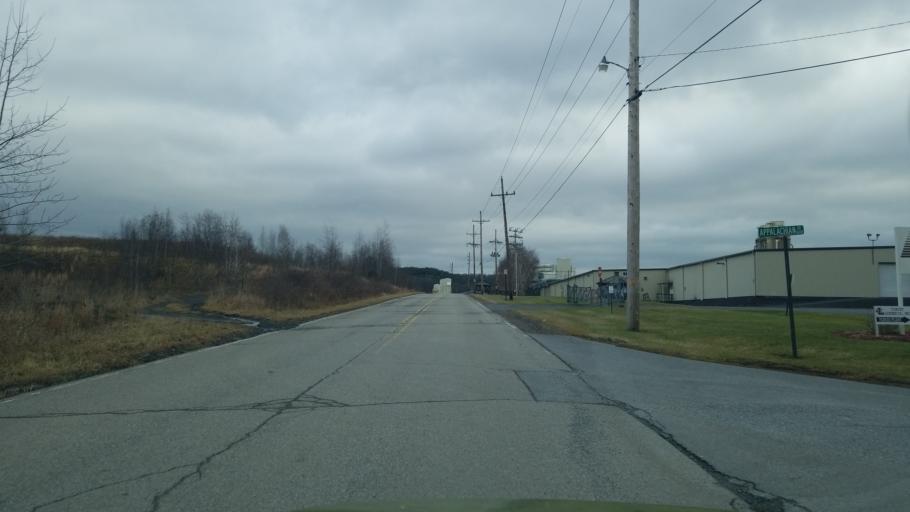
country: US
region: Pennsylvania
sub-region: Clearfield County
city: Clearfield
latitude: 41.0281
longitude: -78.3967
